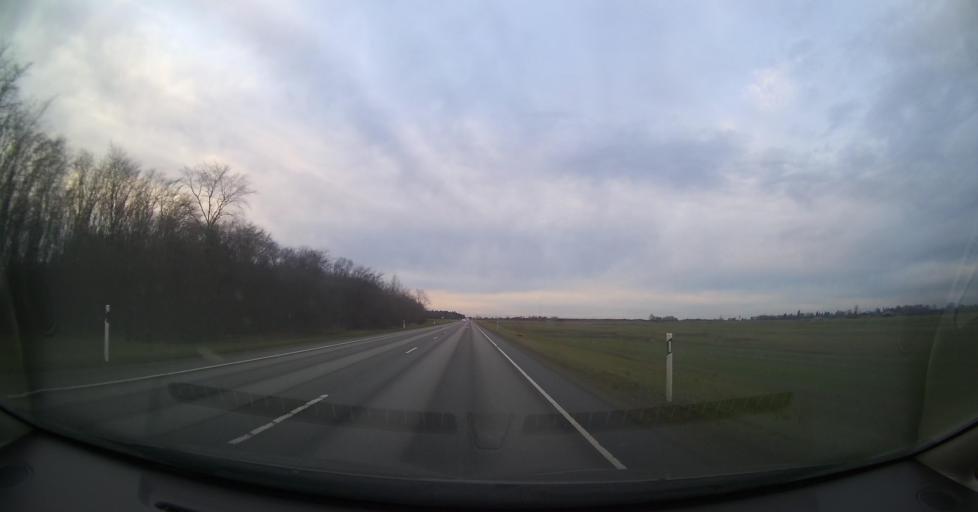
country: EE
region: Ida-Virumaa
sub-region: Kohtla-Jaerve linn
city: Kohtla-Jarve
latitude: 59.4207
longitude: 27.2410
